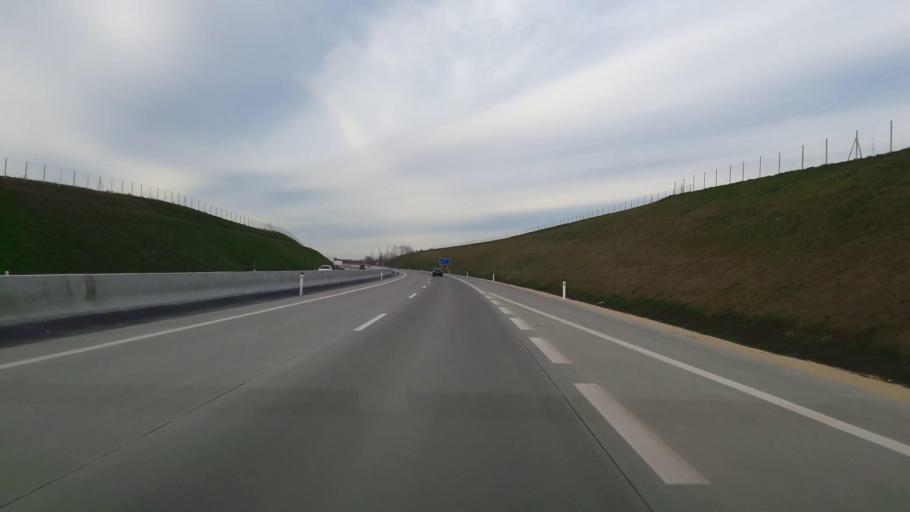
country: AT
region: Lower Austria
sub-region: Politischer Bezirk Mistelbach
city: Herrnbaumgarten
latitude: 48.6552
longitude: 16.6906
